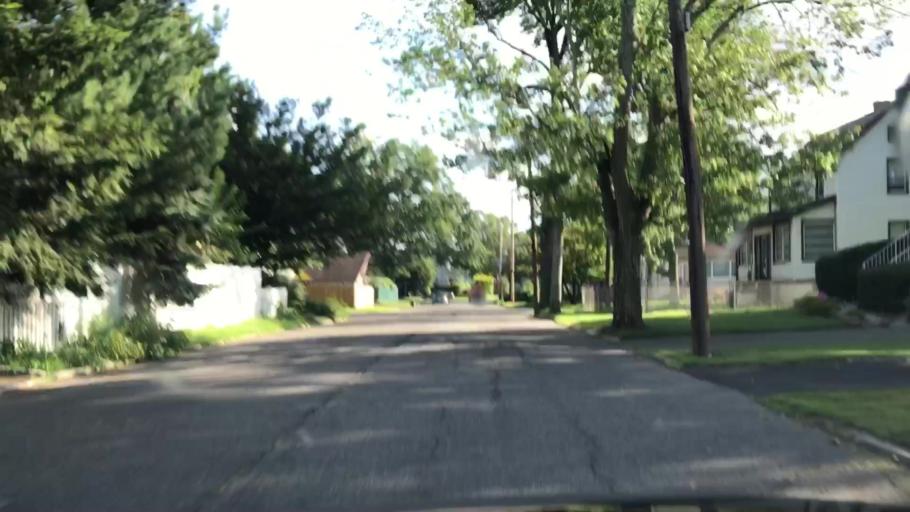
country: US
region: New Jersey
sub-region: Bergen County
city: Dumont
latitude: 40.9383
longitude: -74.0010
